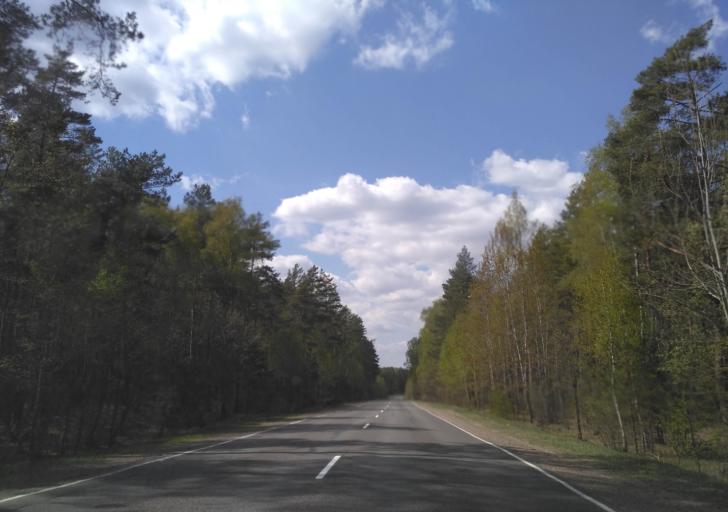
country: BY
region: Minsk
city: Vilyeyka
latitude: 54.4988
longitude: 27.1021
